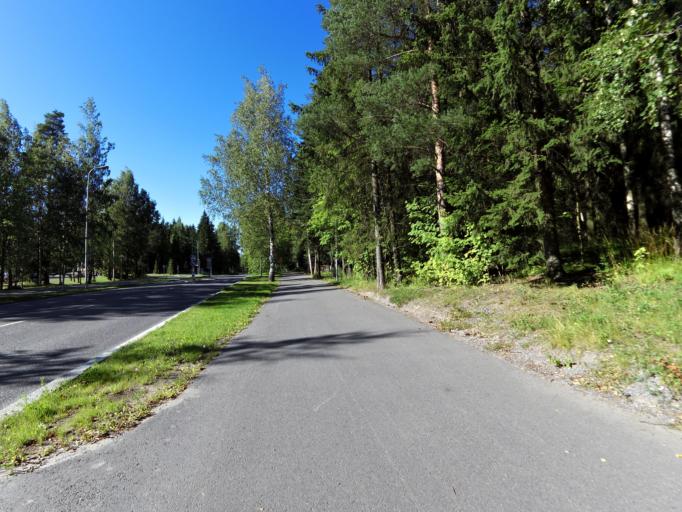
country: FI
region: Pirkanmaa
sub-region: Tampere
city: Pirkkala
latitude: 61.5062
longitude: 23.6288
